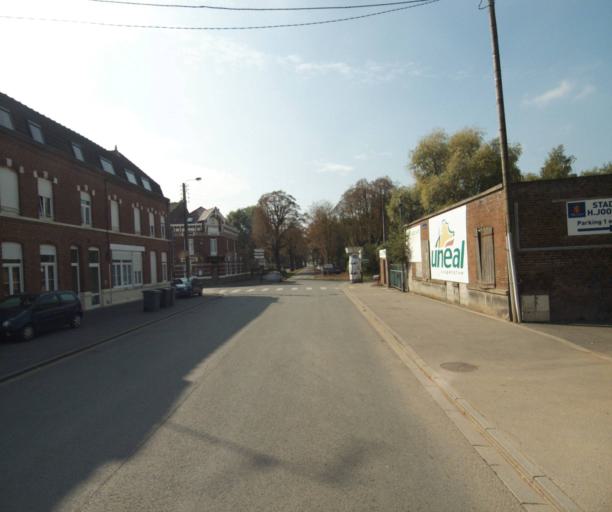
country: FR
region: Nord-Pas-de-Calais
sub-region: Departement du Nord
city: Seclin
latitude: 50.5492
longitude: 3.0234
